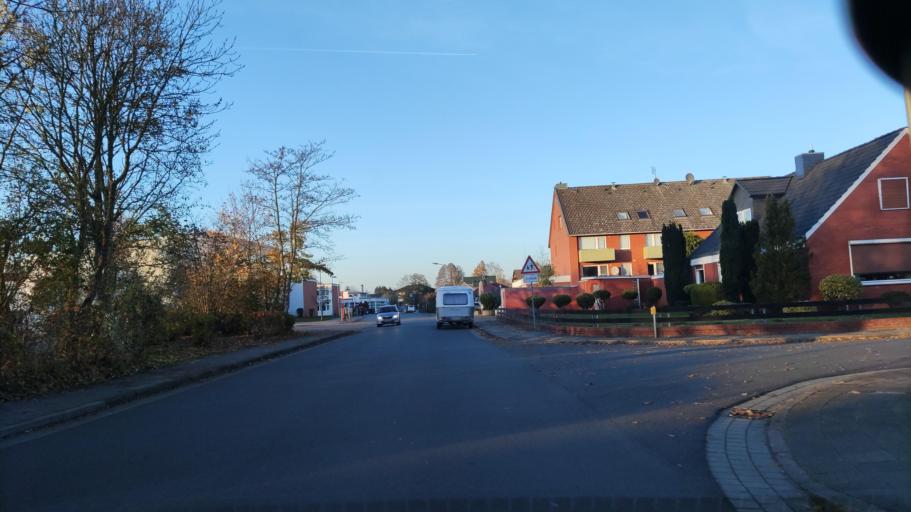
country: DE
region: Lower Saxony
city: Bleckede
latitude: 53.2846
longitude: 10.7314
